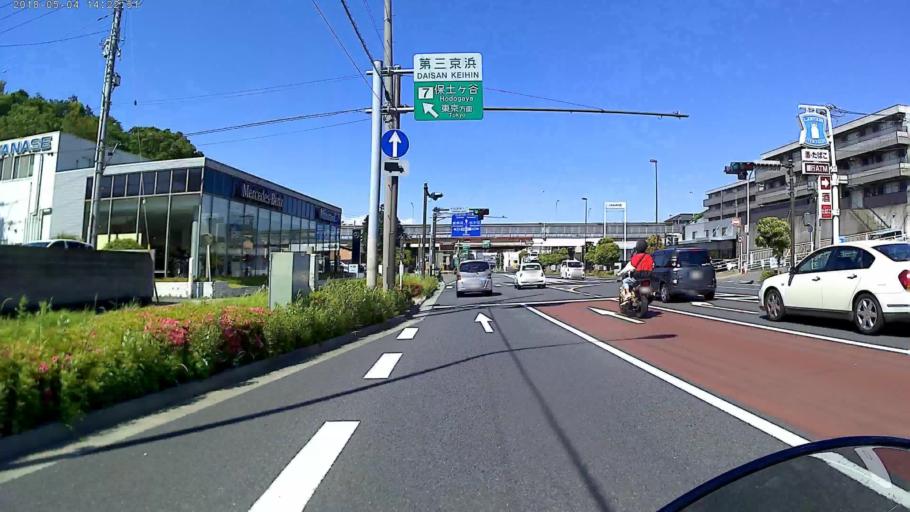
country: JP
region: Kanagawa
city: Yokohama
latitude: 35.4735
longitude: 139.5986
